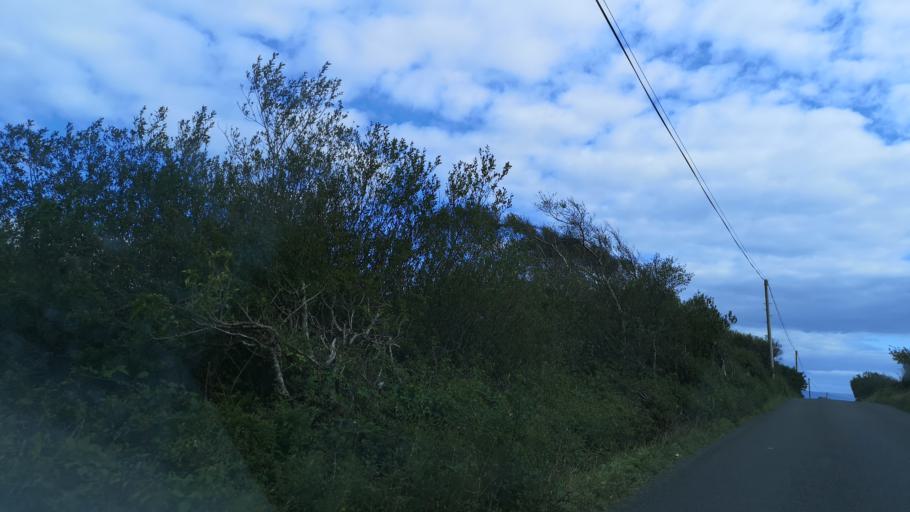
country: IE
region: Connaught
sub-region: County Galway
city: Bearna
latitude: 53.2735
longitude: -9.1606
